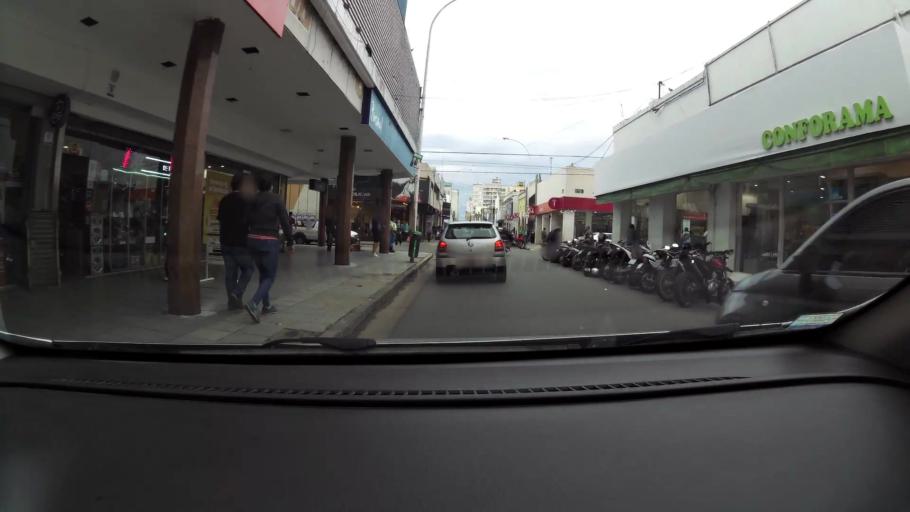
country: AR
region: Buenos Aires
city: San Nicolas de los Arroyos
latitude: -33.3326
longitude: -60.2209
